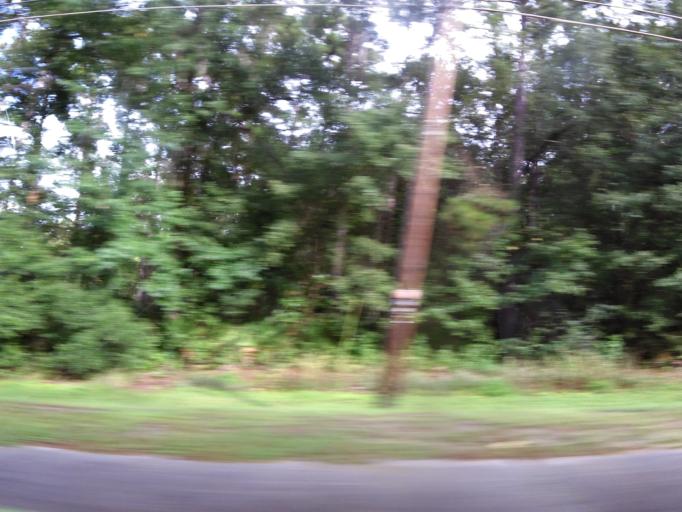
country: US
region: Georgia
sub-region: Liberty County
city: Walthourville
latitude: 31.7914
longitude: -81.6080
